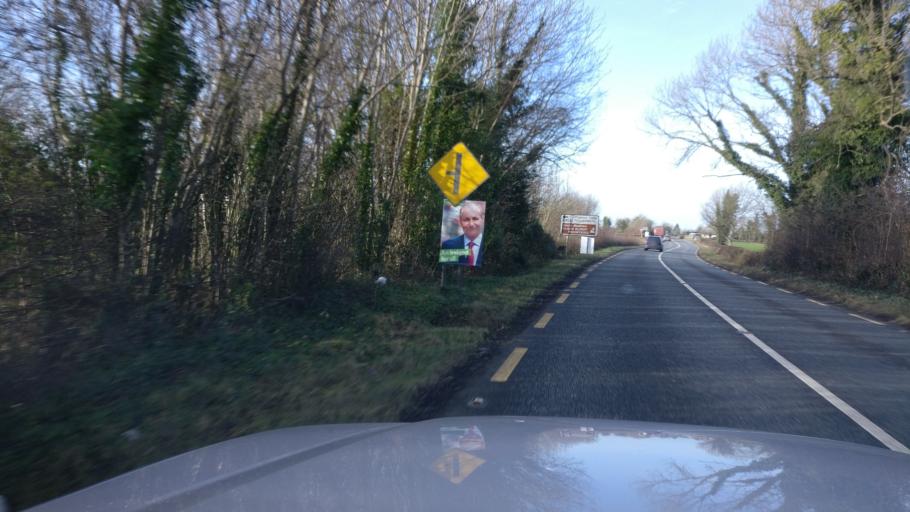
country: IE
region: Leinster
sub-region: Laois
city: Mountmellick
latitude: 53.1455
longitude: -7.3667
